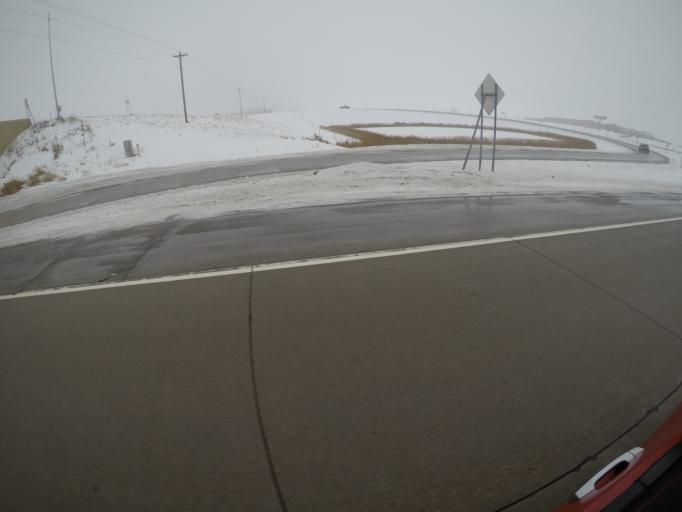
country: US
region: Minnesota
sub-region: Olmsted County
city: Oronoco
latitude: 44.0945
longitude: -92.5120
